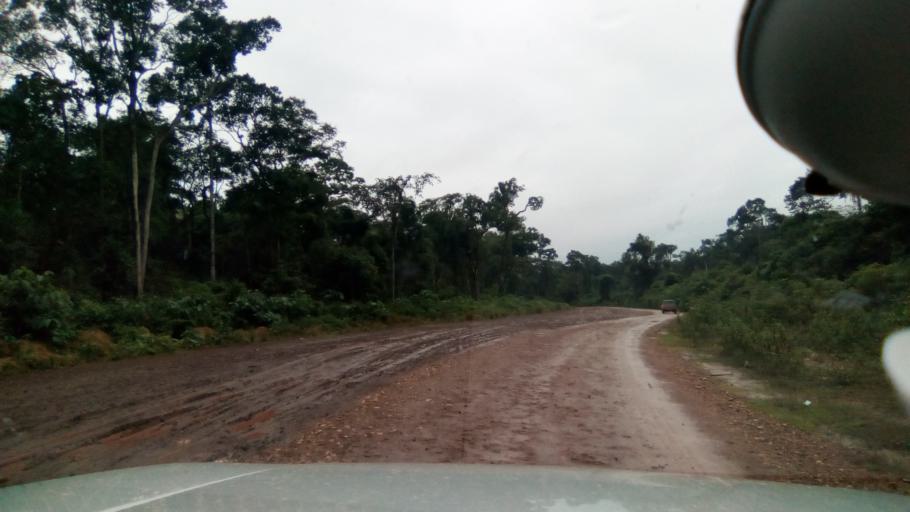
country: LA
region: Attapu
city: Attapu
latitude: 14.6813
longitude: 106.5569
